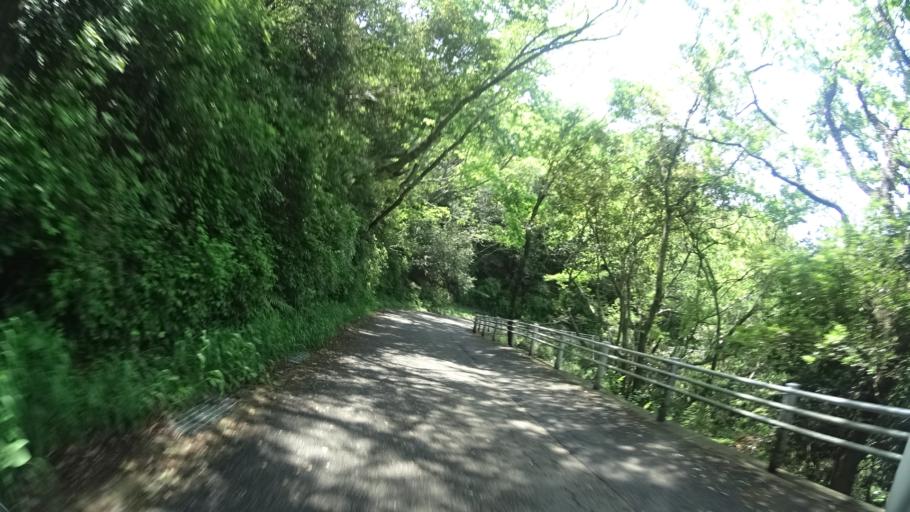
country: JP
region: Tokushima
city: Tokushima-shi
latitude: 34.0676
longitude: 134.5234
